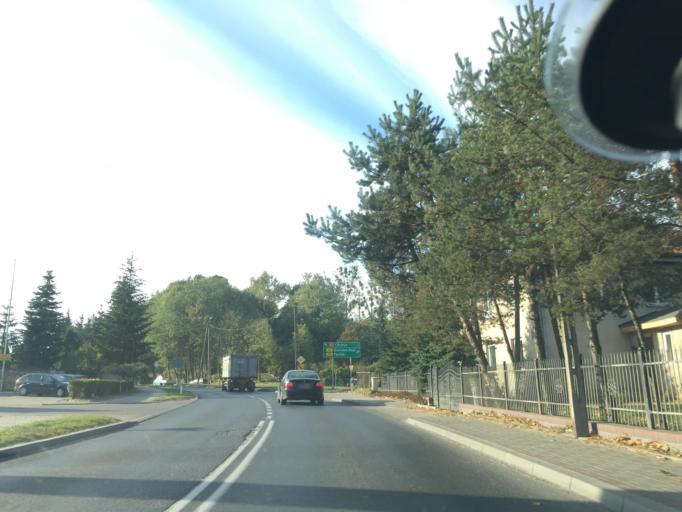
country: PL
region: Warmian-Masurian Voivodeship
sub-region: Powiat lidzbarski
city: Lidzbark Warminski
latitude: 54.1220
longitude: 20.5736
